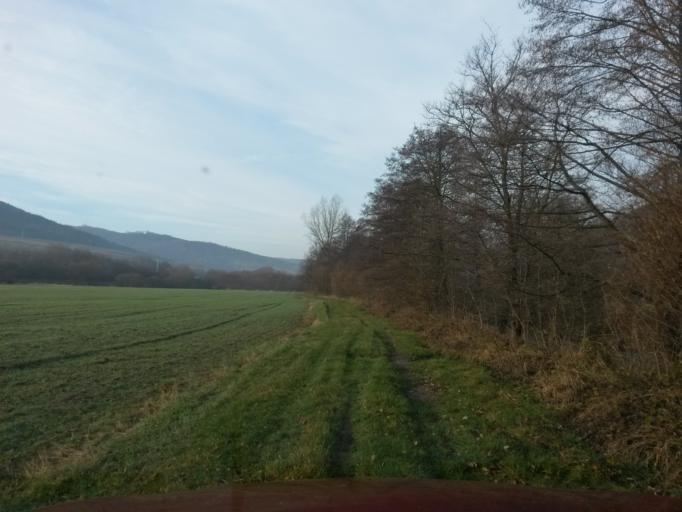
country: SK
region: Kosicky
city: Roznava
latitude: 48.7116
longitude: 20.4592
